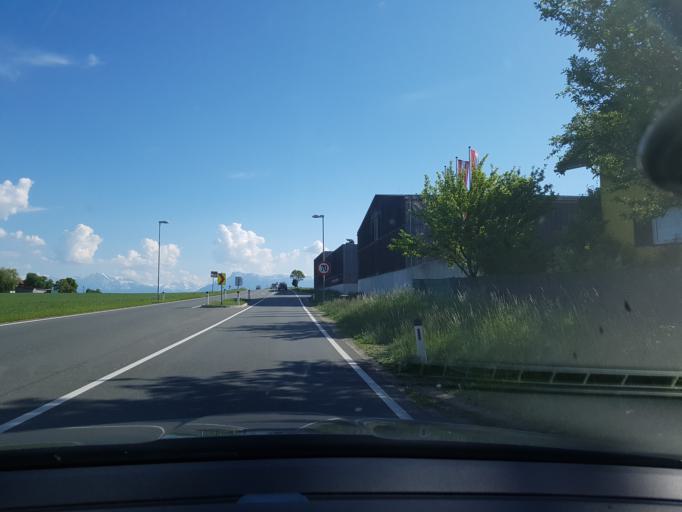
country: AT
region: Salzburg
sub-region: Politischer Bezirk Salzburg-Umgebung
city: Obertrum am See
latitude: 47.9075
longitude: 13.0810
